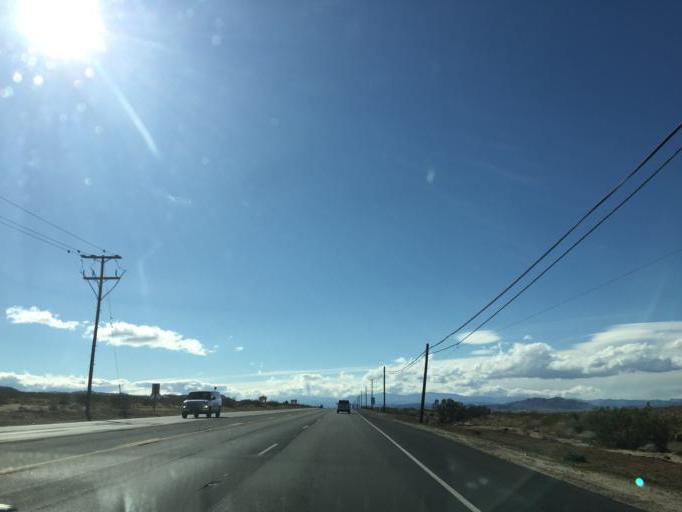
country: US
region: California
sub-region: San Bernardino County
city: Joshua Tree
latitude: 34.1352
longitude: -116.1932
